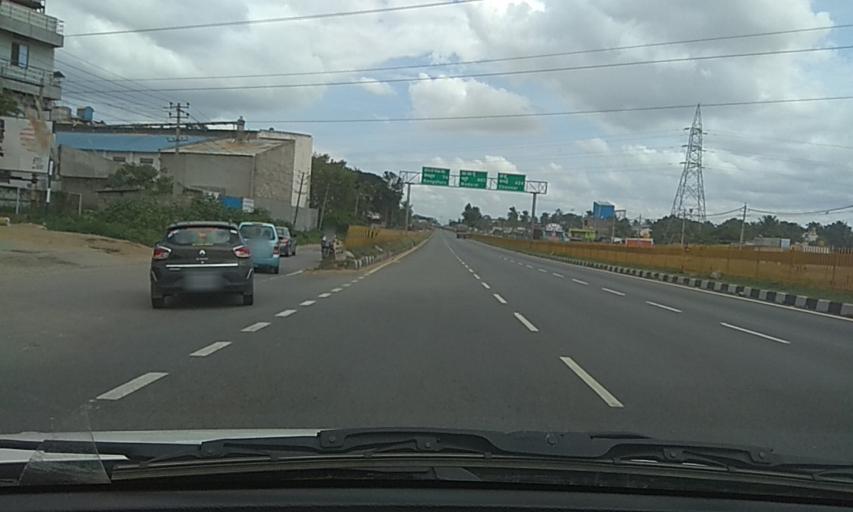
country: IN
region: Karnataka
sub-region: Tumkur
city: Tumkur
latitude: 13.3857
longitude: 77.0953
